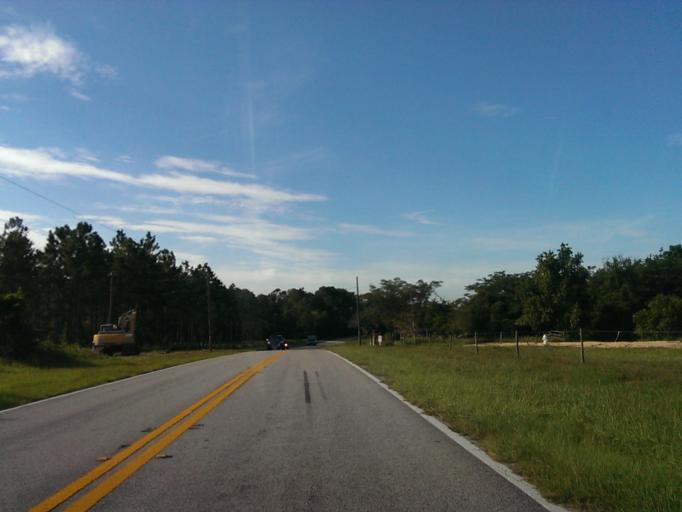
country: US
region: Florida
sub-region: Polk County
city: Citrus Ridge
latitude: 28.4097
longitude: -81.6358
